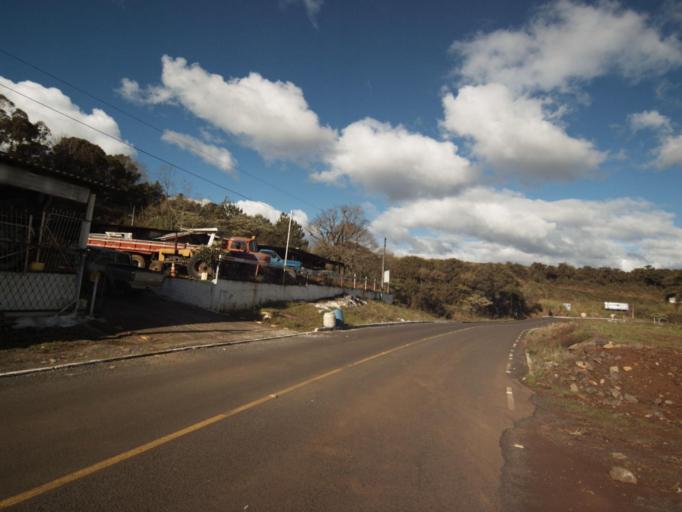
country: BR
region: Santa Catarina
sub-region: Joacaba
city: Joacaba
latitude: -27.1662
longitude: -51.5610
